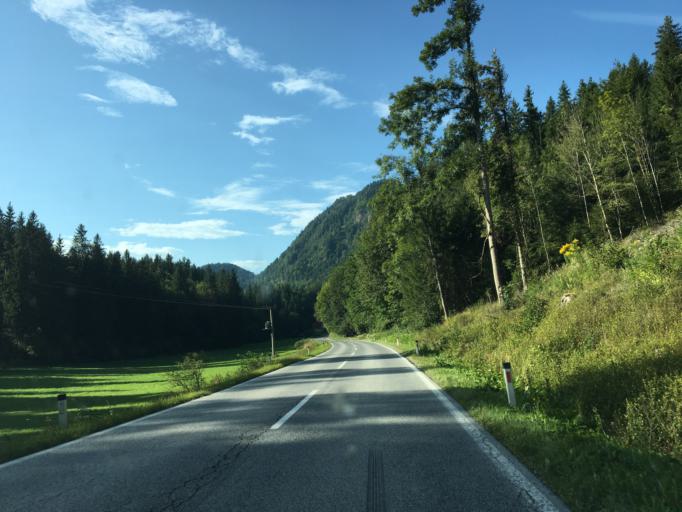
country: AT
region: Carinthia
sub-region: Politischer Bezirk Sankt Veit an der Glan
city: Bruckl
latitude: 46.7121
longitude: 14.5636
